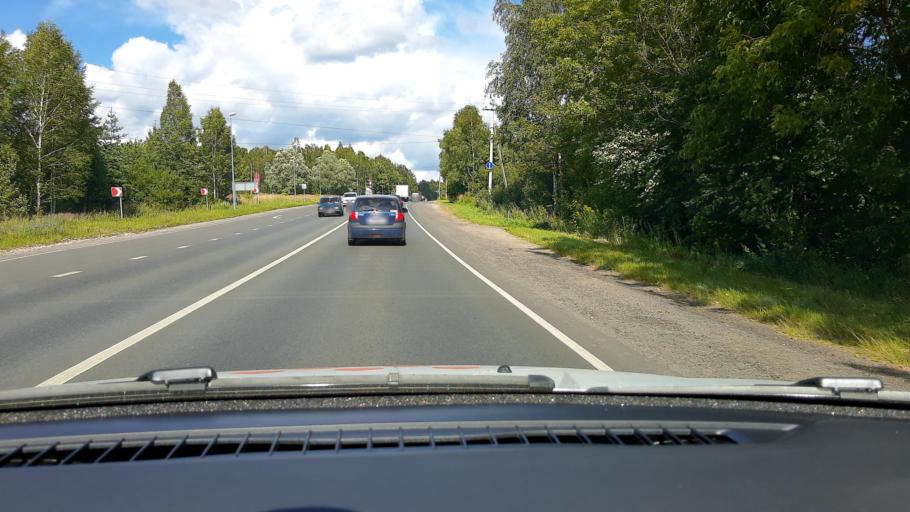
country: RU
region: Nizjnij Novgorod
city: Bogorodsk
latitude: 56.1294
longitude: 43.6048
